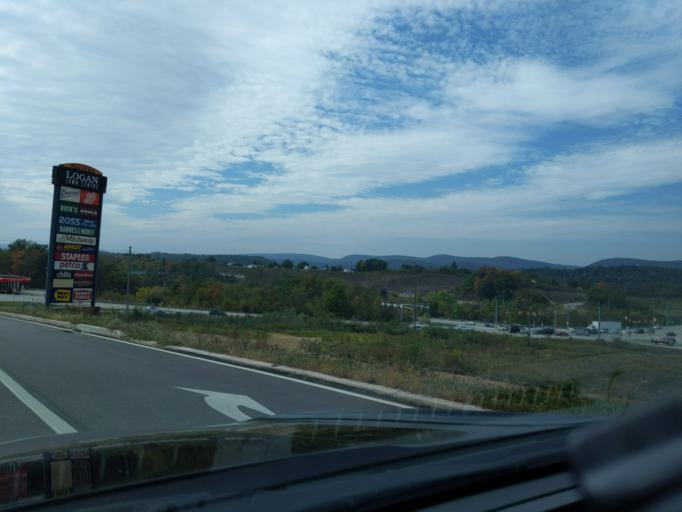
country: US
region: Pennsylvania
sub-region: Blair County
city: Lakemont
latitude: 40.4787
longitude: -78.3896
